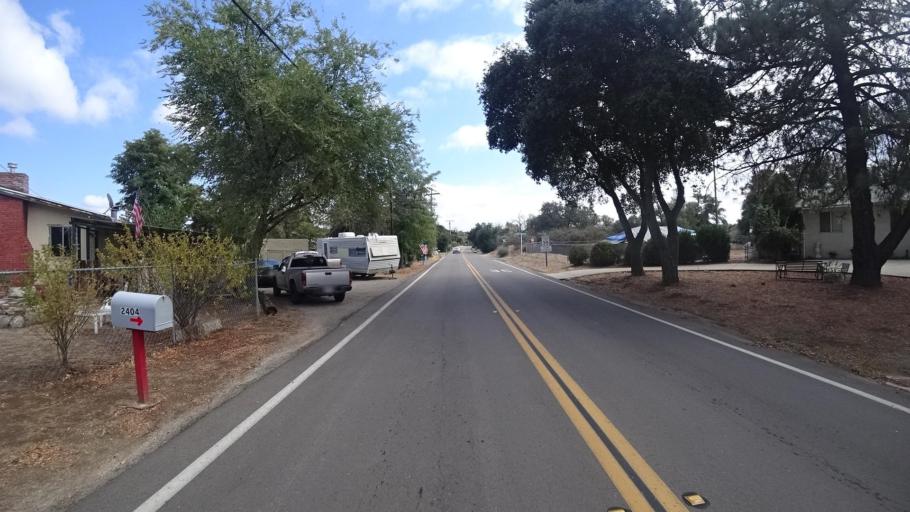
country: US
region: California
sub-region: San Diego County
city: Campo
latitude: 32.6790
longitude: -116.5105
